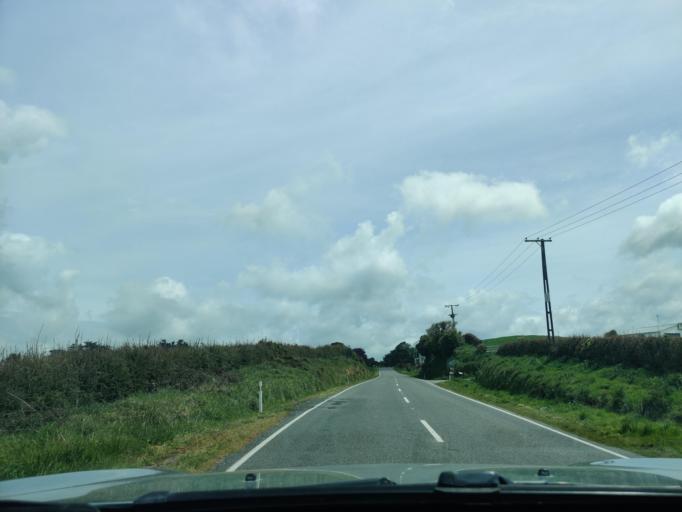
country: NZ
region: Taranaki
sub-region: South Taranaki District
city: Eltham
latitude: -39.3766
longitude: 174.1771
